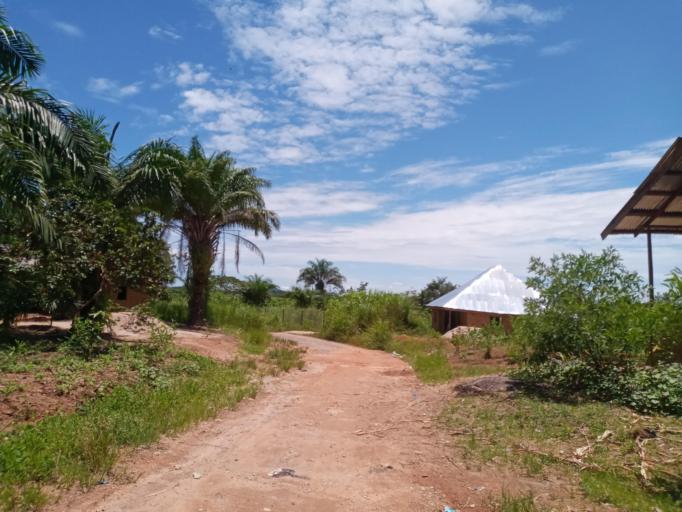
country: SL
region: Eastern Province
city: Koidu
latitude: 8.6516
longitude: -10.9518
